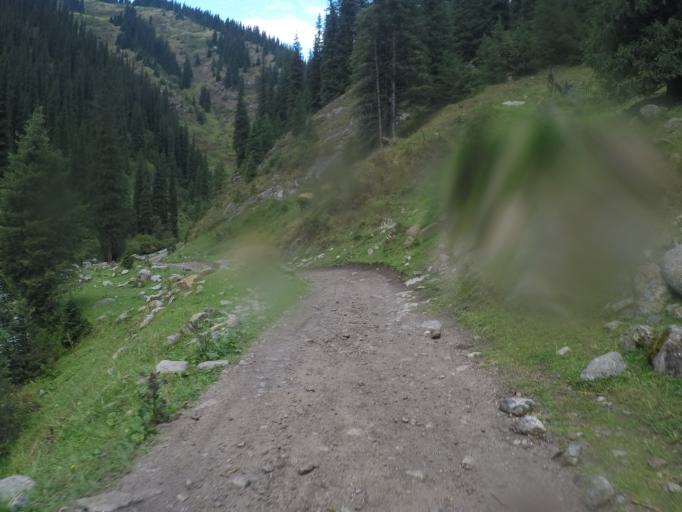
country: KG
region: Ysyk-Koel
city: Teploklyuchenka
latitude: 42.4137
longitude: 78.5731
